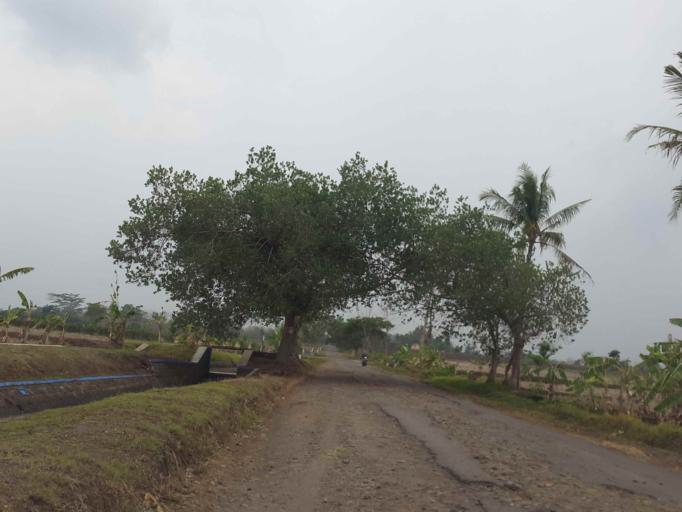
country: ID
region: Central Java
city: Selogiri
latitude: -7.7170
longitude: 110.9556
